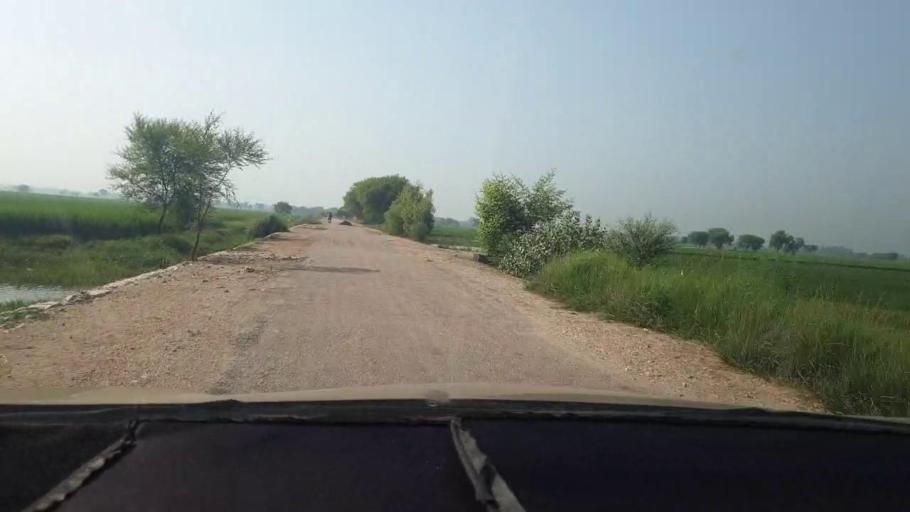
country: PK
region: Sindh
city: Kambar
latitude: 27.6235
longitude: 68.0897
